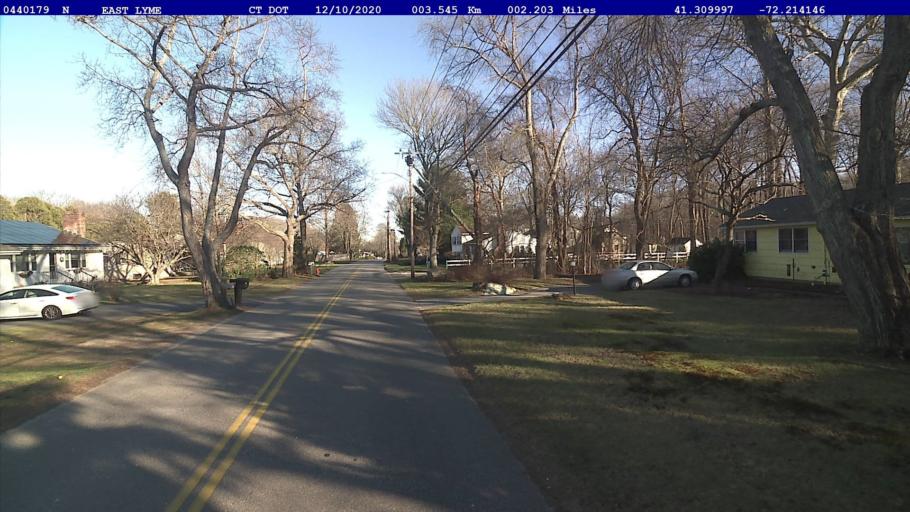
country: US
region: Connecticut
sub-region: New London County
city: Niantic
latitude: 41.3100
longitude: -72.2141
